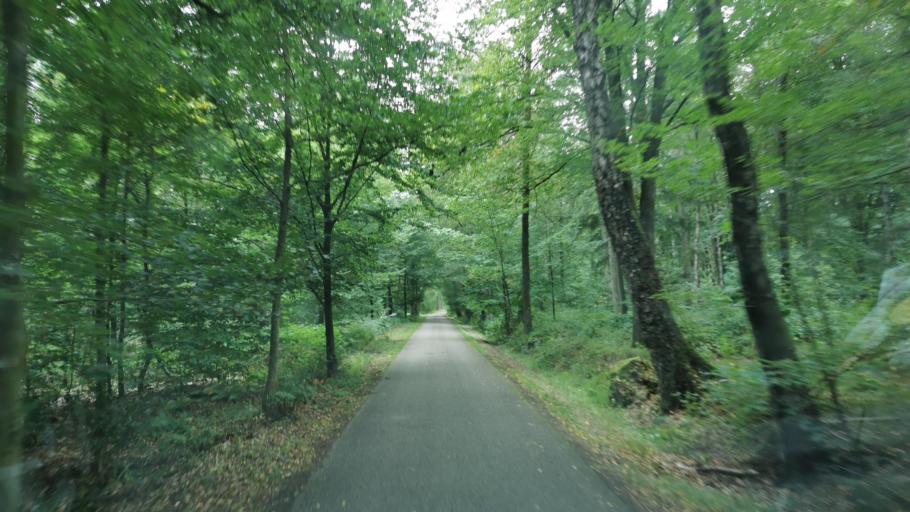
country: NL
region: Overijssel
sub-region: Gemeente Oldenzaal
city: Oldenzaal
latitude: 52.3358
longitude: 6.9804
